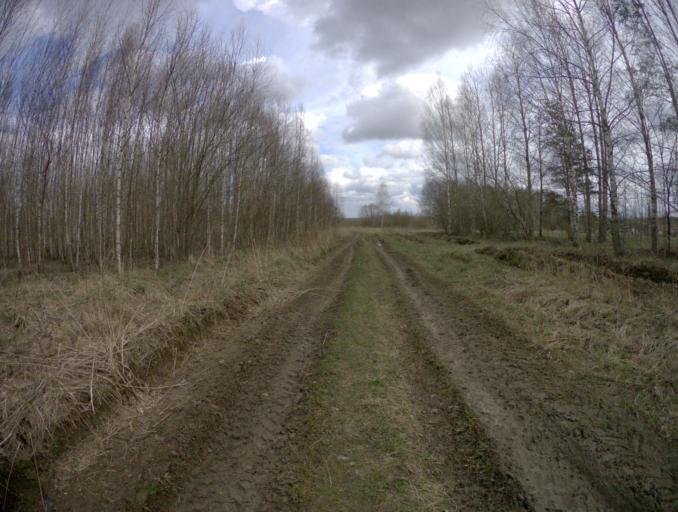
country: RU
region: Vladimir
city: Orgtrud
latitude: 56.0748
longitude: 40.7366
